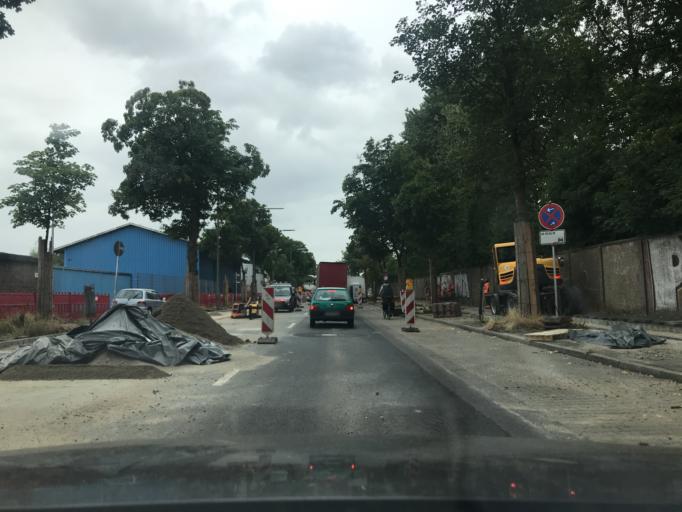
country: DE
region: North Rhine-Westphalia
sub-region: Regierungsbezirk Dusseldorf
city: Erkrath
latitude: 51.1838
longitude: 6.8557
